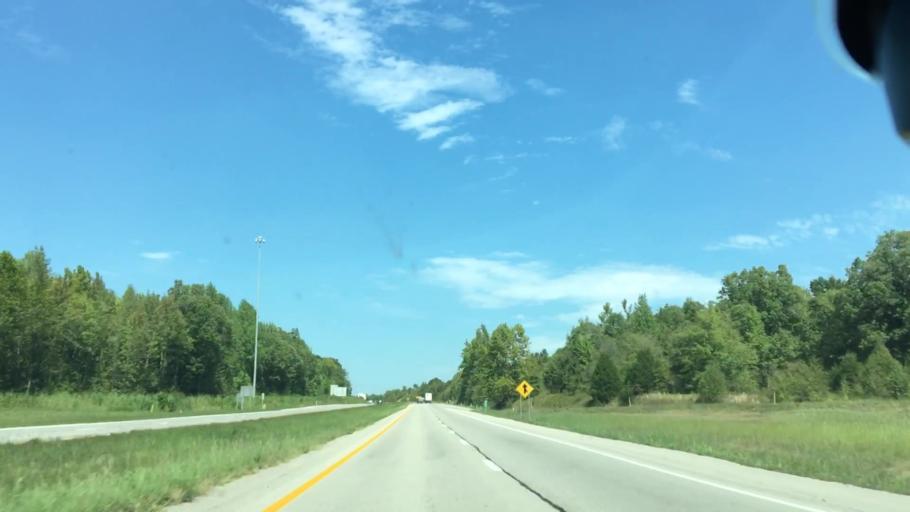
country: US
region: Kentucky
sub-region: Hopkins County
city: Nortonville
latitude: 37.1930
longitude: -87.4414
